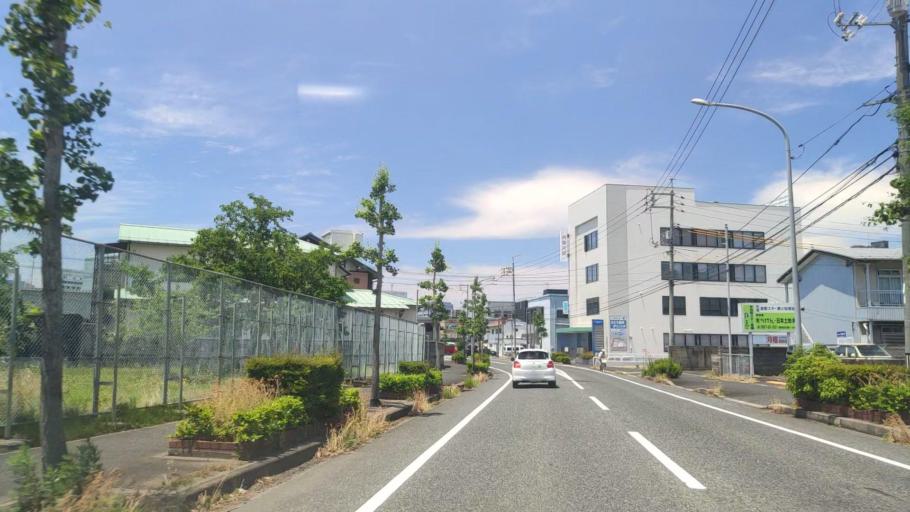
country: JP
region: Tottori
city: Tottori
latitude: 35.4898
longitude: 134.2316
